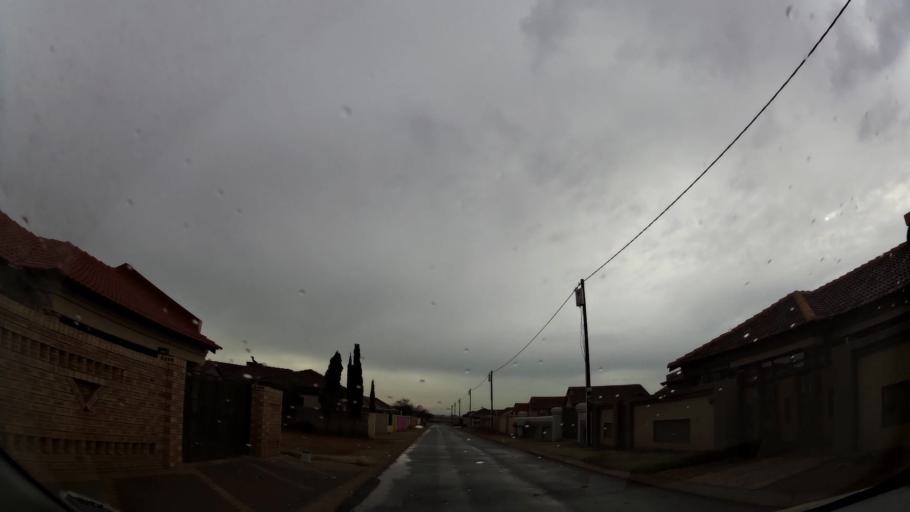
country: ZA
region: Gauteng
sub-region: Ekurhuleni Metropolitan Municipality
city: Germiston
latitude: -26.3332
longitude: 28.1987
